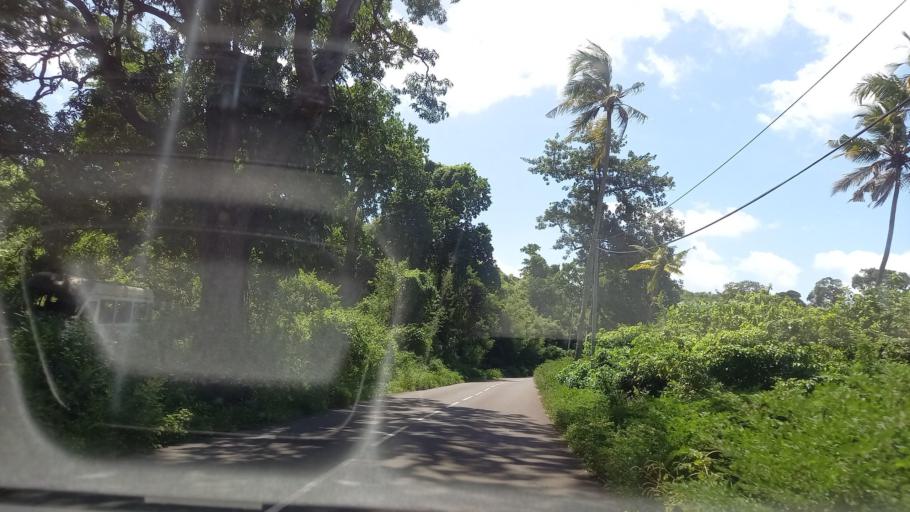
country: YT
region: Bandraboua
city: Bandraboua
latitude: -12.6866
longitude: 45.1040
